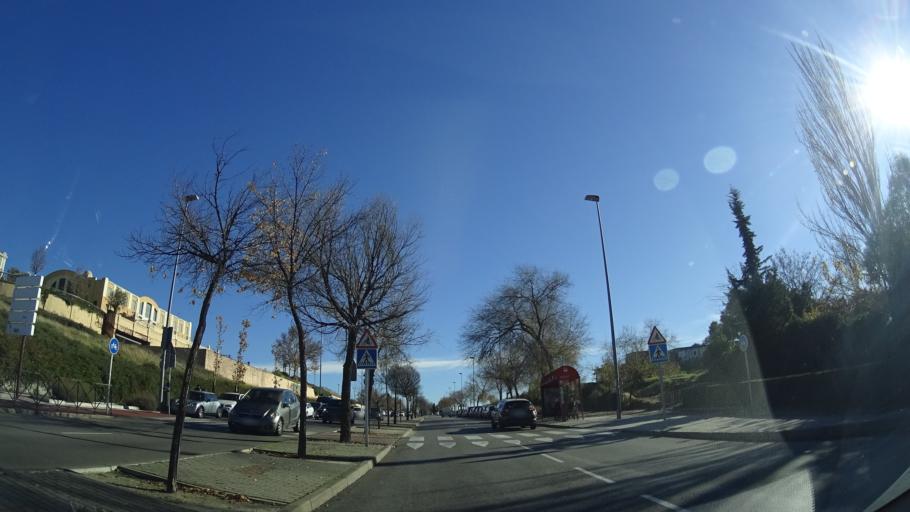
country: ES
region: Madrid
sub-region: Provincia de Madrid
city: Las Rozas de Madrid
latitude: 40.5180
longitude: -3.9041
